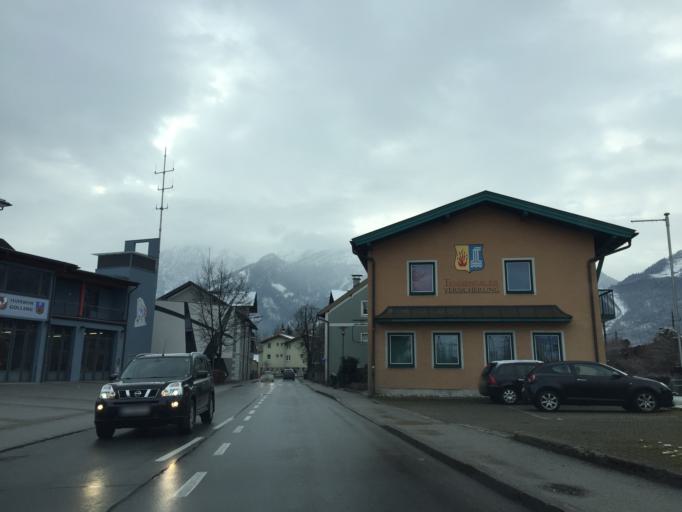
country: AT
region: Salzburg
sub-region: Politischer Bezirk Hallein
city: Golling an der Salzach
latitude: 47.5966
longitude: 13.1663
